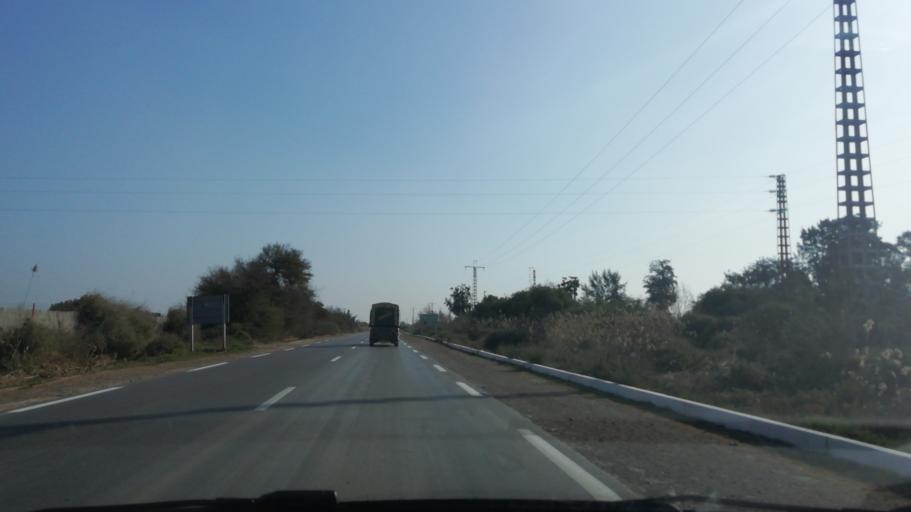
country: DZ
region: Mostaganem
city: Mostaganem
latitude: 35.7433
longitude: 0.0118
